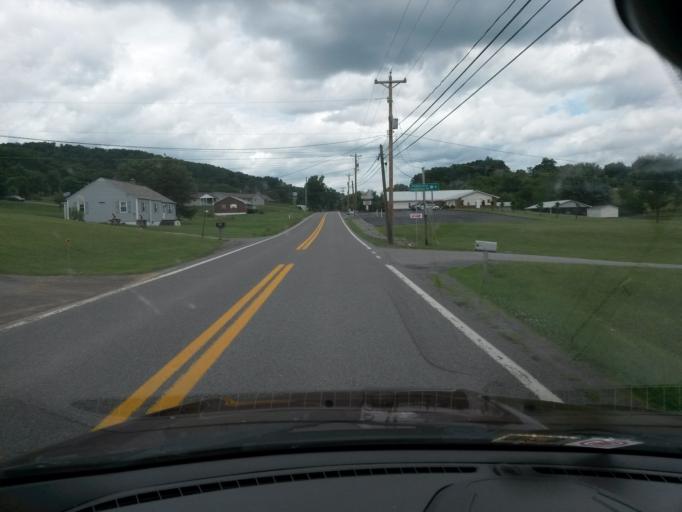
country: US
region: Virginia
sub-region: Giles County
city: Pearisburg
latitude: 37.4063
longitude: -80.7579
